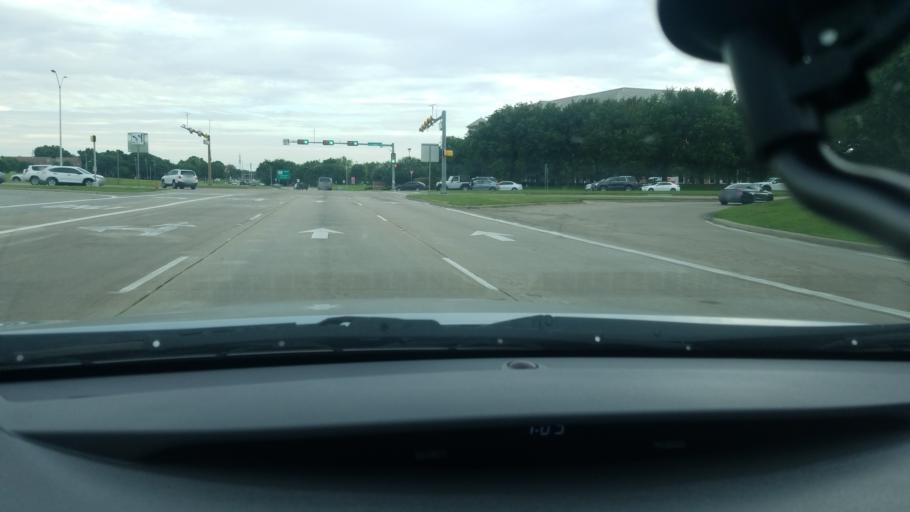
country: US
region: Texas
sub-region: Collin County
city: Frisco
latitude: 33.0714
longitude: -96.7967
